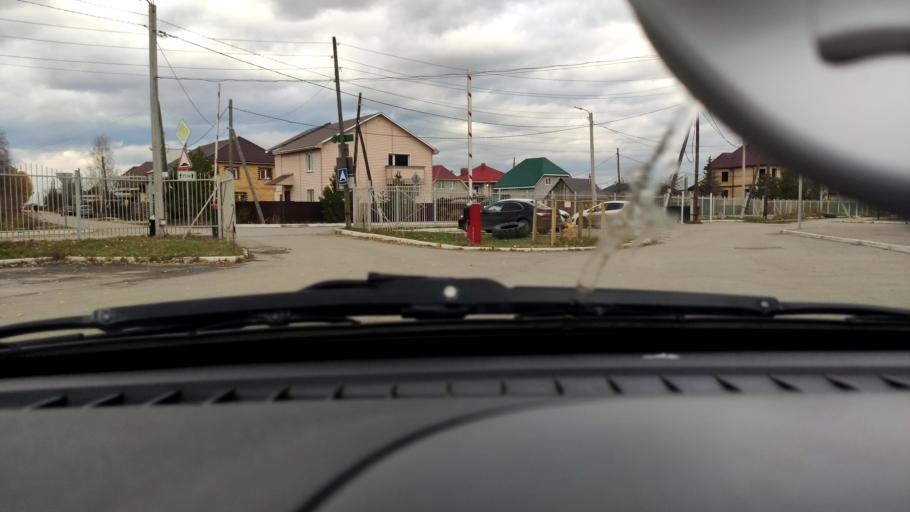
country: RU
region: Perm
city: Kondratovo
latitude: 57.9779
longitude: 56.0997
